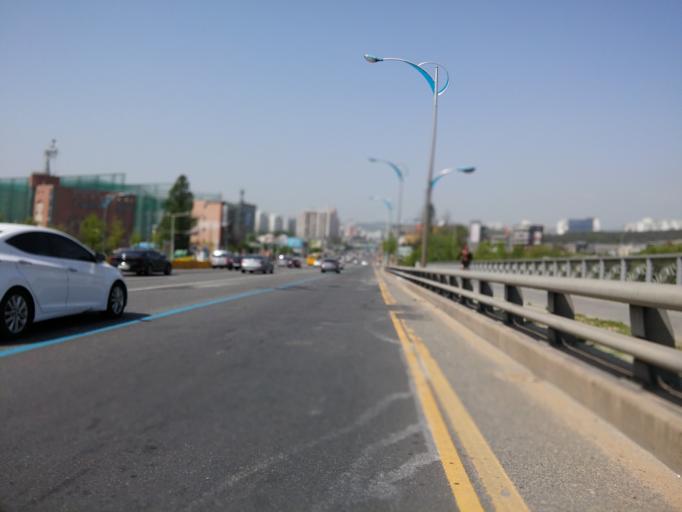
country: KR
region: Daejeon
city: Daejeon
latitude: 36.3067
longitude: 127.3589
